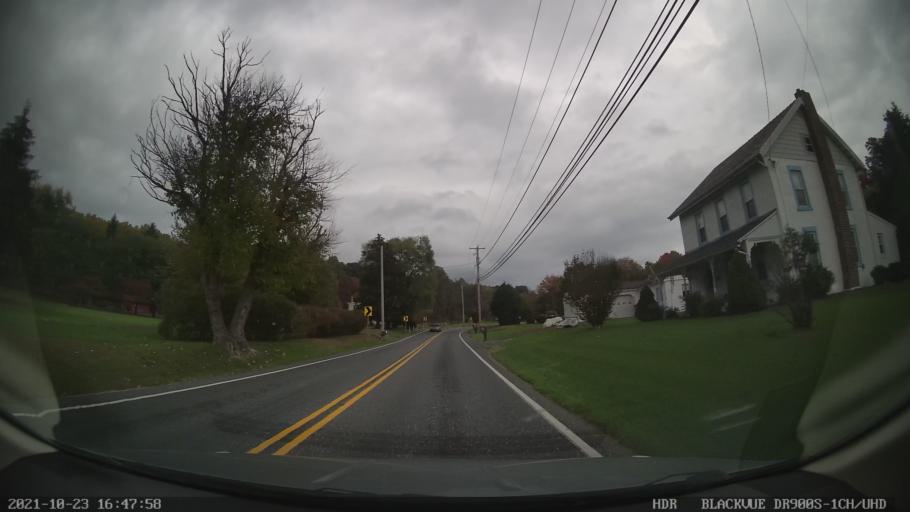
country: US
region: Pennsylvania
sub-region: Berks County
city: Red Lion
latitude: 40.4914
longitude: -75.6301
